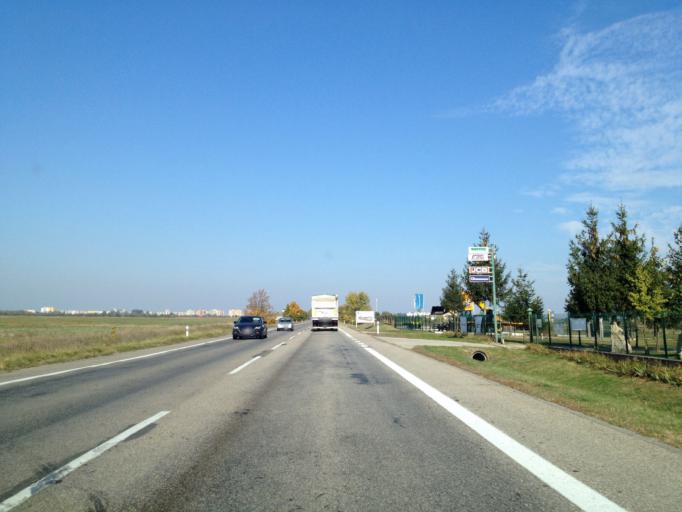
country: SK
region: Nitriansky
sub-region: Okres Nove Zamky
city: Nove Zamky
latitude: 47.9556
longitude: 18.1911
